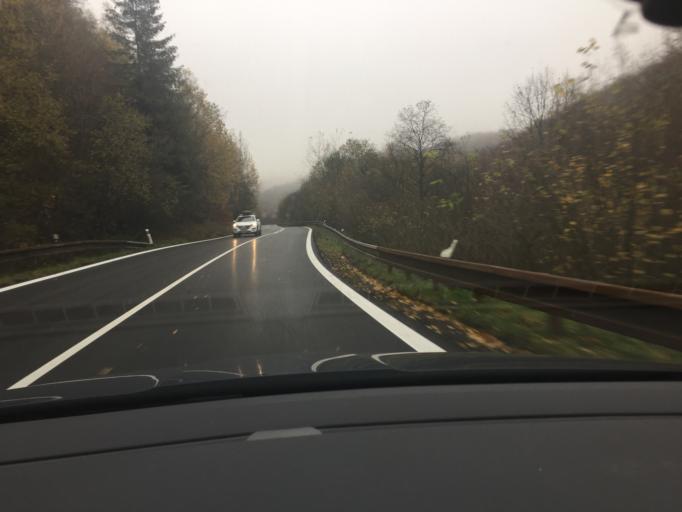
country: PL
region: Lesser Poland Voivodeship
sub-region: Powiat nowosadecki
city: Tylicz
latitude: 49.3034
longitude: 20.9956
